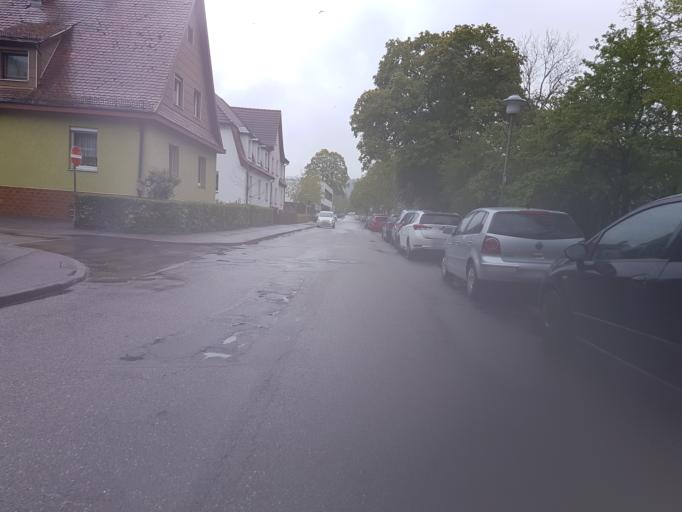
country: DE
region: Baden-Wuerttemberg
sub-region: Freiburg Region
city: Oberndorf
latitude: 48.2969
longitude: 8.5774
